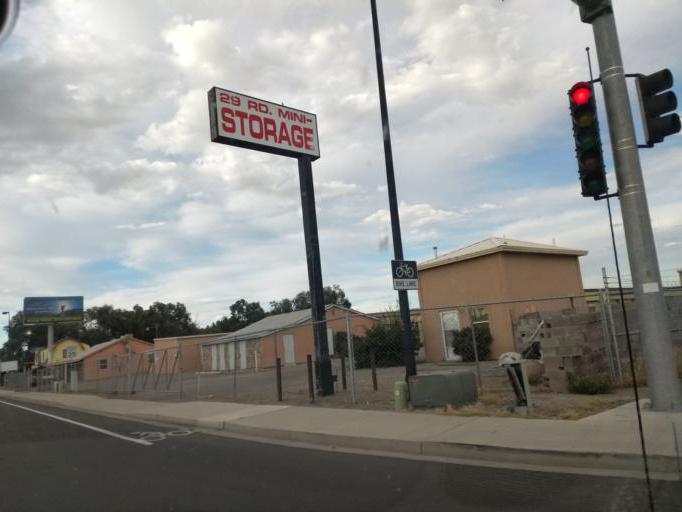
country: US
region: Colorado
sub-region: Mesa County
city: Fruitvale
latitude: 39.0755
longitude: -108.5151
